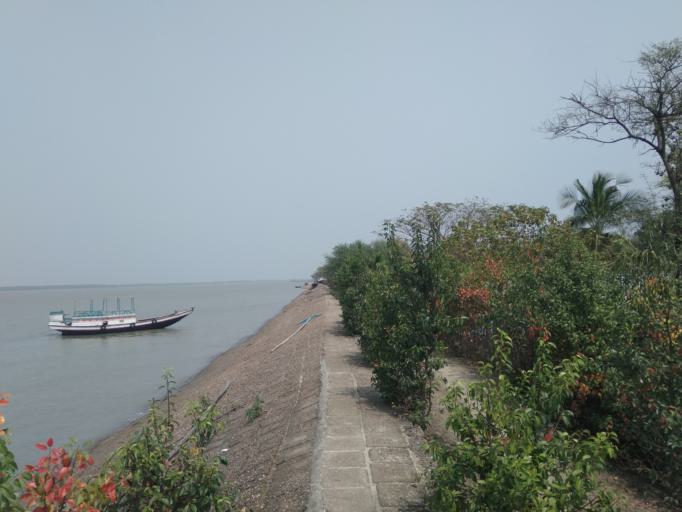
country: IN
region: West Bengal
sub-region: North 24 Parganas
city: Gosaba
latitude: 22.2525
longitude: 89.2504
